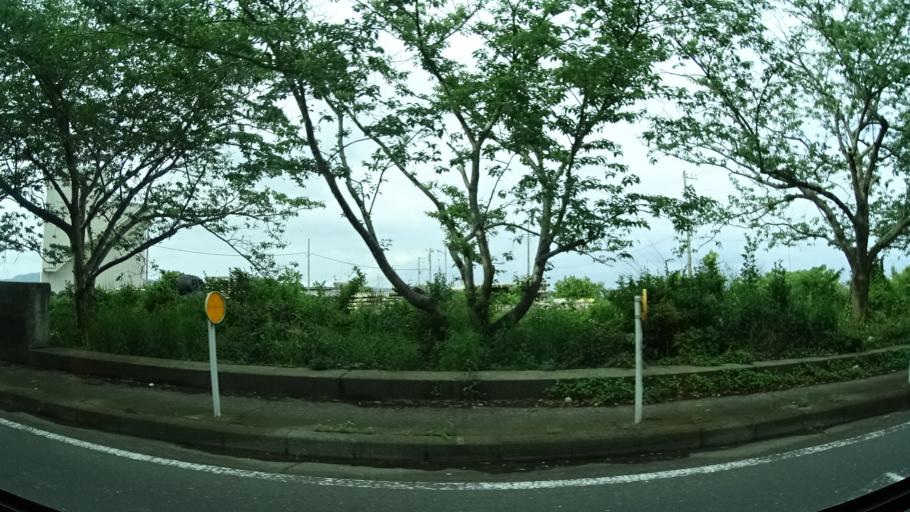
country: JP
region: Kanagawa
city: Miura
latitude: 35.1582
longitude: 139.6664
